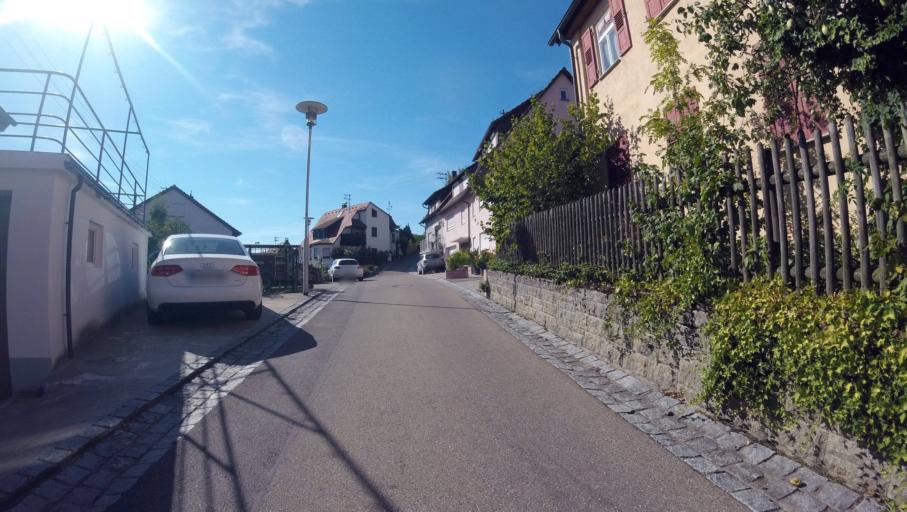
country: DE
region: Baden-Wuerttemberg
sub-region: Regierungsbezirk Stuttgart
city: Kirchberg an der Murr
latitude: 48.9429
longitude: 9.3376
